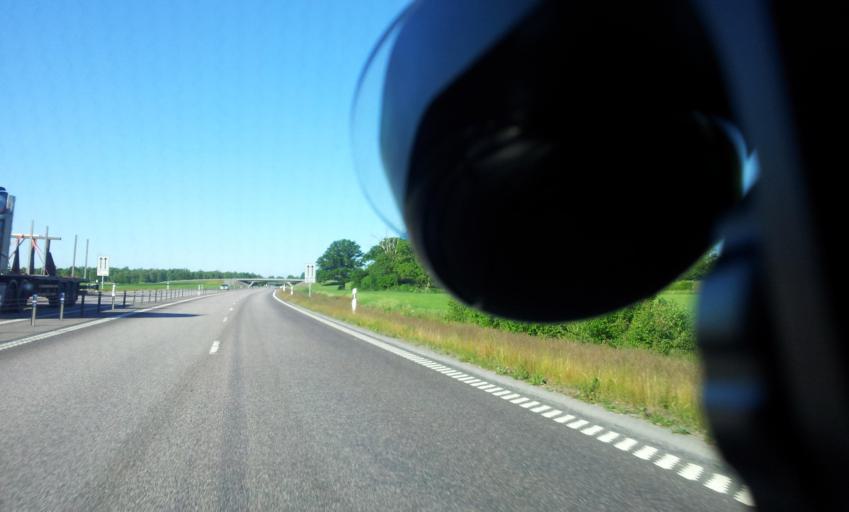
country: SE
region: Kalmar
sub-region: Kalmar Kommun
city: Ljungbyholm
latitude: 56.5788
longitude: 16.1125
